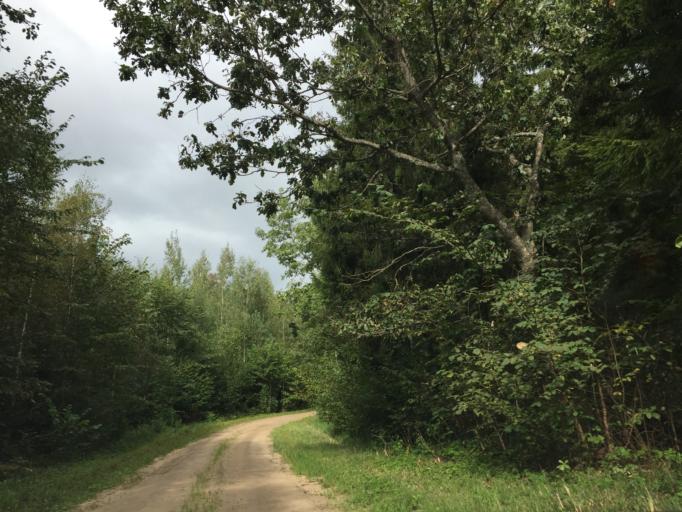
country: LV
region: Pargaujas
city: Stalbe
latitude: 57.5012
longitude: 24.9182
